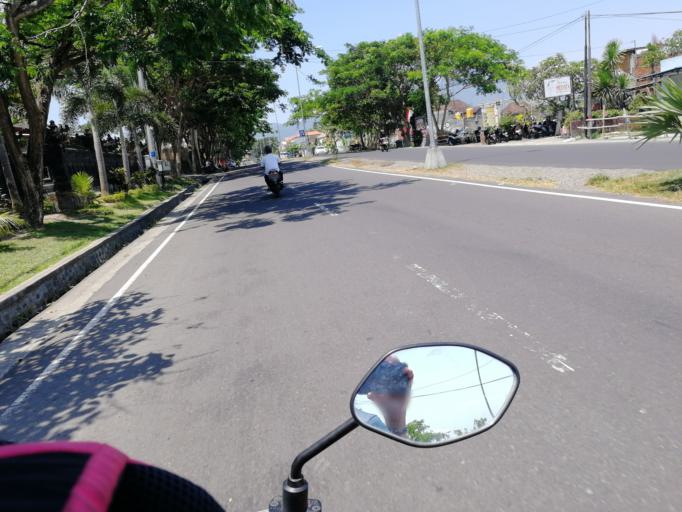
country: ID
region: Bali
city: Subagan
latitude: -8.4431
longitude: 115.5904
